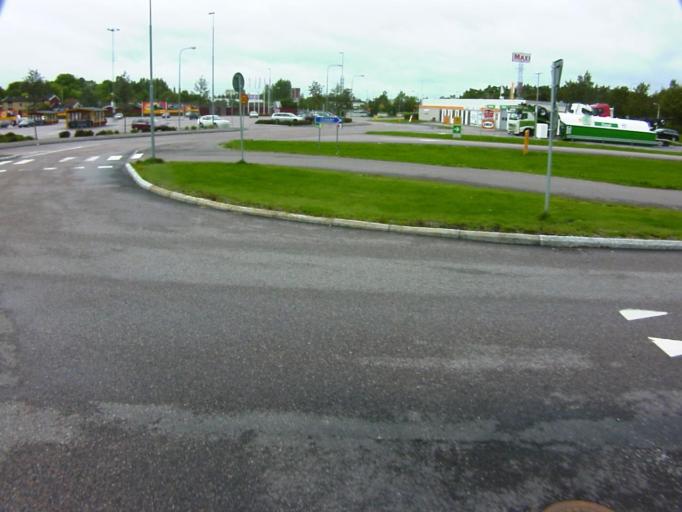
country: SE
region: Soedermanland
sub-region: Eskilstuna Kommun
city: Eskilstuna
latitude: 59.3895
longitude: 16.5337
